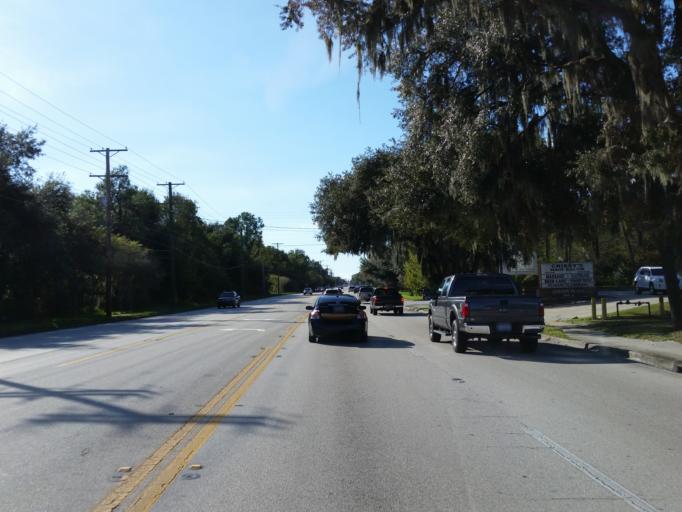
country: US
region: Florida
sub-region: Hillsborough County
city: Bloomingdale
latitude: 27.8937
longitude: -82.2784
